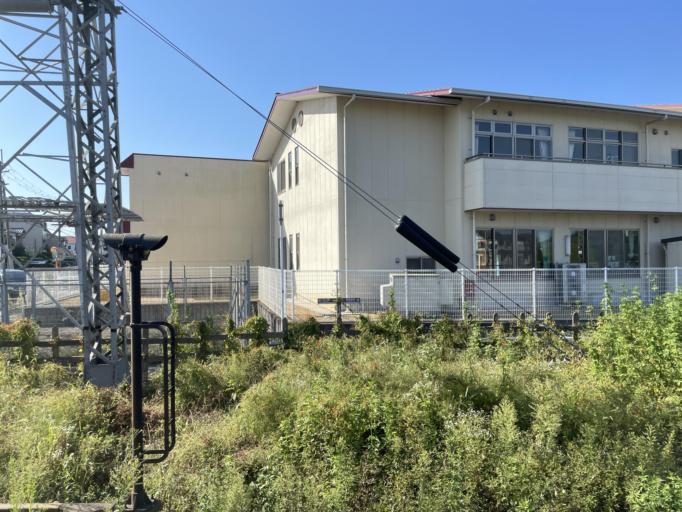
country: JP
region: Nara
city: Gose
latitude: 34.5087
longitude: 135.7156
